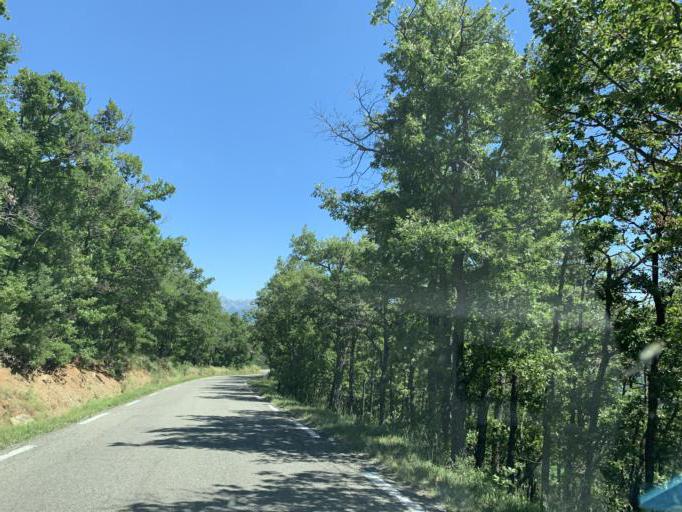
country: FR
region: Provence-Alpes-Cote d'Azur
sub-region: Departement des Hautes-Alpes
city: La Batie-Neuve
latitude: 44.5869
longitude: 6.1600
